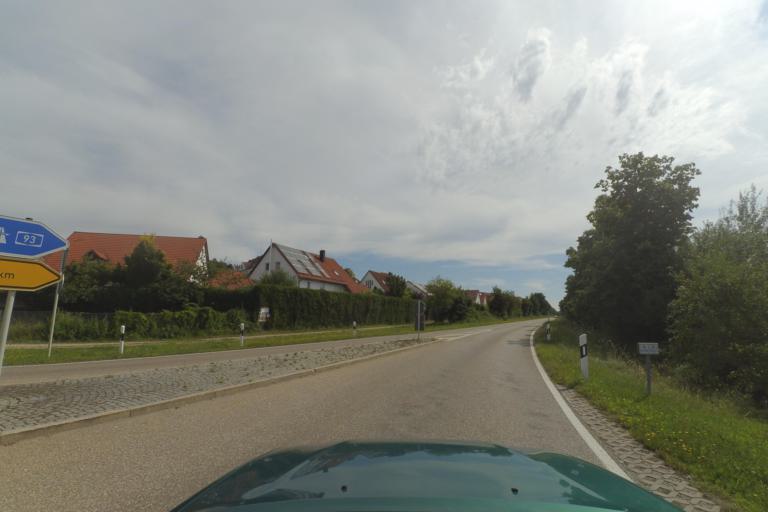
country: DE
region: Bavaria
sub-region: Lower Bavaria
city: Bad Abbach
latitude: 48.9360
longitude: 12.0631
